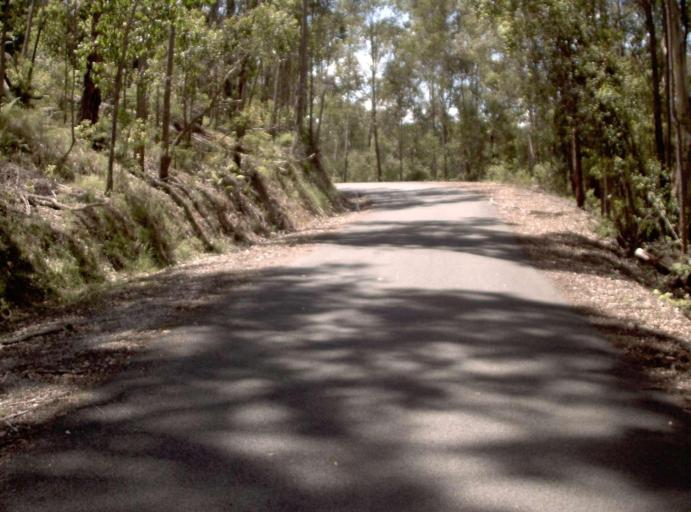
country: AU
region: New South Wales
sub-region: Bombala
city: Bombala
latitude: -37.5033
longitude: 148.9249
